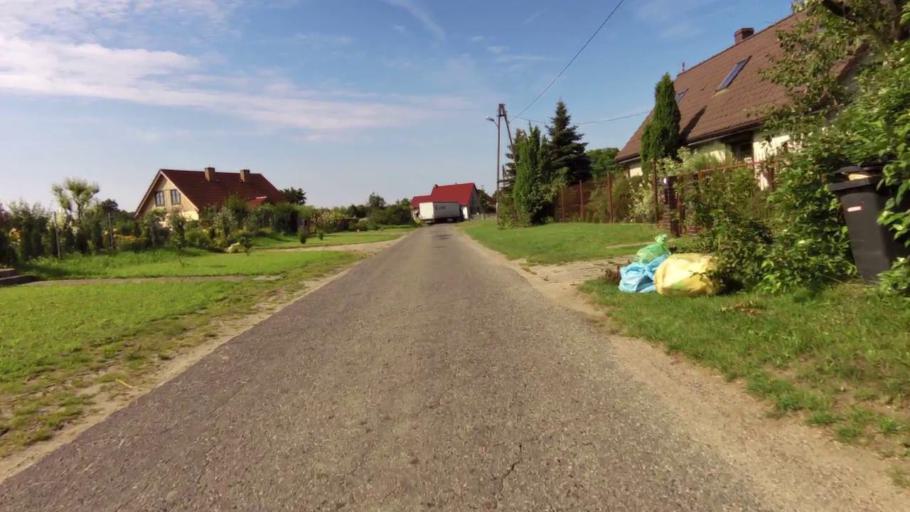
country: PL
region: West Pomeranian Voivodeship
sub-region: Powiat stargardzki
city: Marianowo
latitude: 53.3456
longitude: 15.1940
